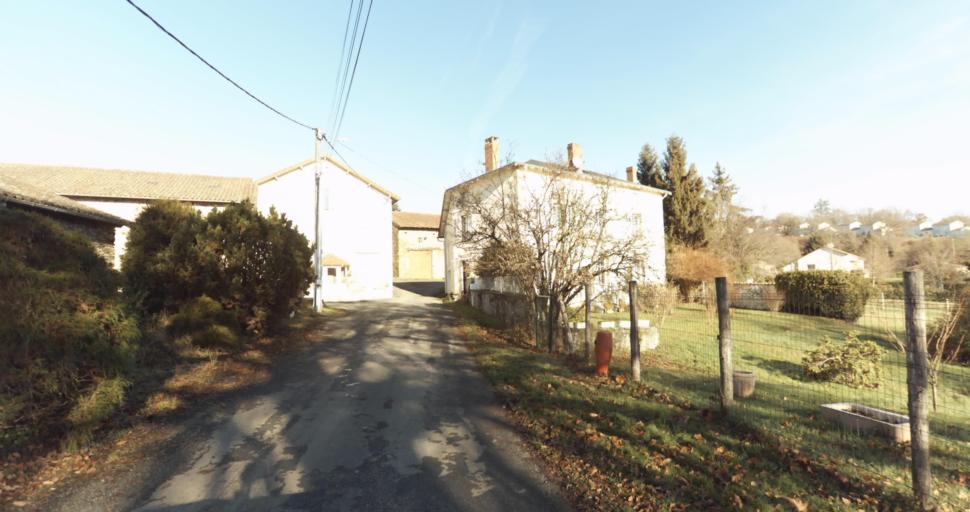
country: FR
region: Limousin
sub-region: Departement de la Haute-Vienne
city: Aixe-sur-Vienne
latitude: 45.8053
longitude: 1.1504
